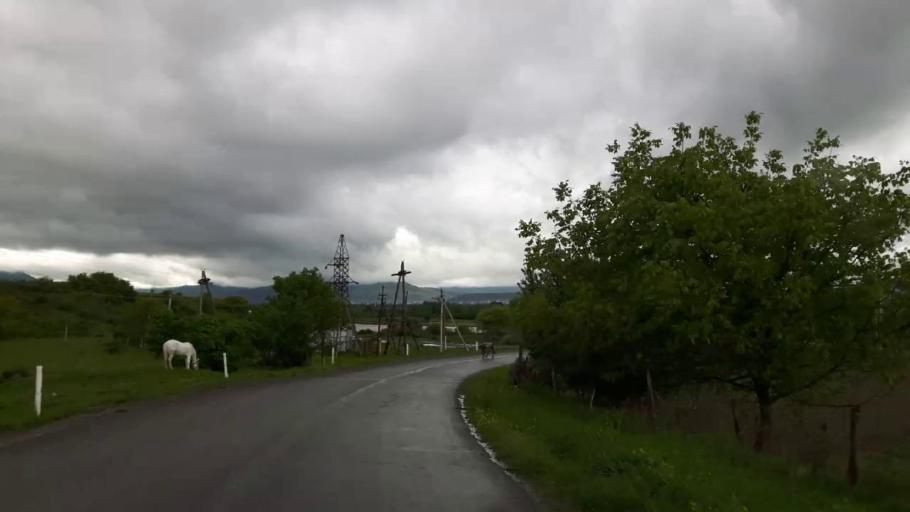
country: GE
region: Shida Kartli
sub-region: Khashuris Raioni
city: Khashuri
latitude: 41.9886
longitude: 43.6607
